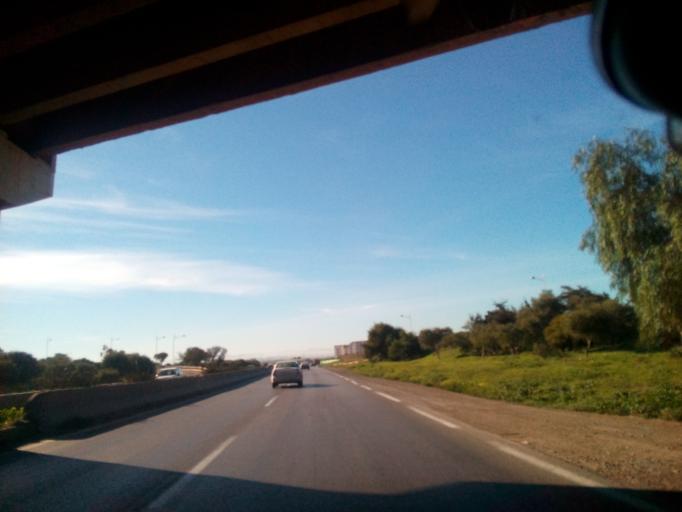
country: DZ
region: Oran
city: Ain el Bya
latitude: 35.7856
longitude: -0.4112
